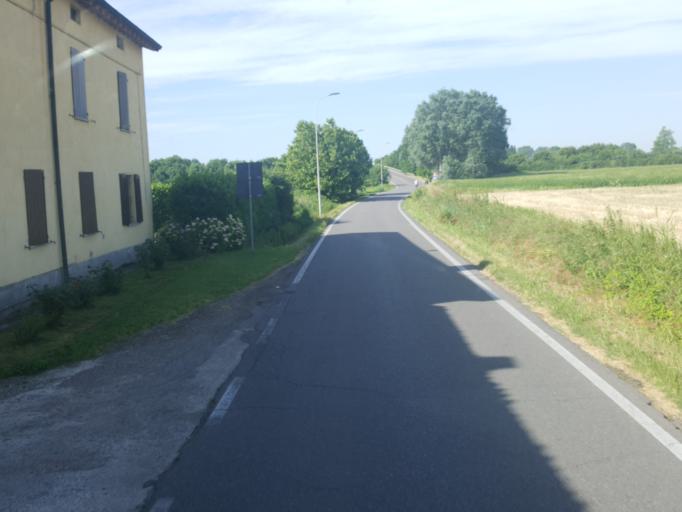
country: IT
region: Lombardy
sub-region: Provincia di Cremona
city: Crema
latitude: 45.3508
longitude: 9.6707
